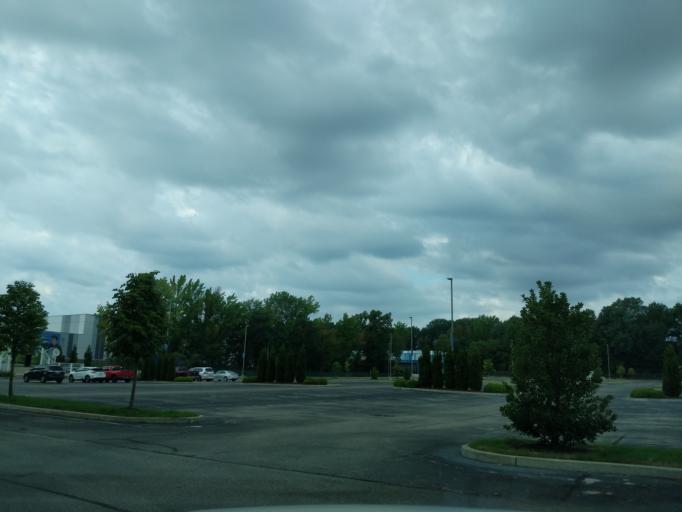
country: US
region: Tennessee
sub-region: Shelby County
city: New South Memphis
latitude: 35.0477
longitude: -90.0267
